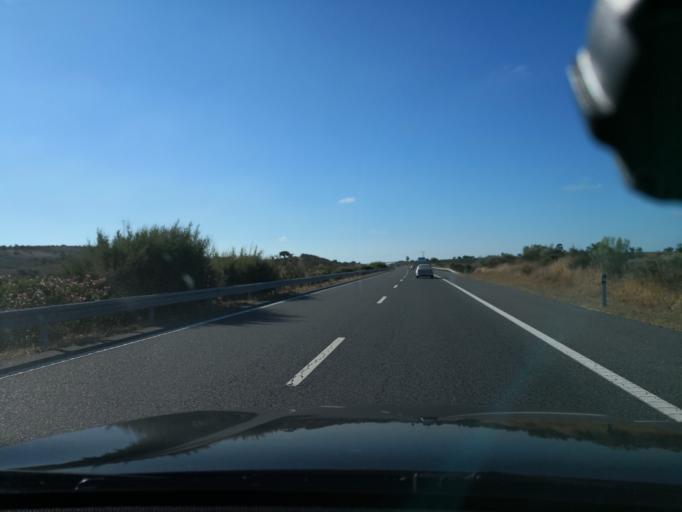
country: PT
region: Beja
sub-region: Ourique
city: Ourique
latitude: 37.7117
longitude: -8.1899
